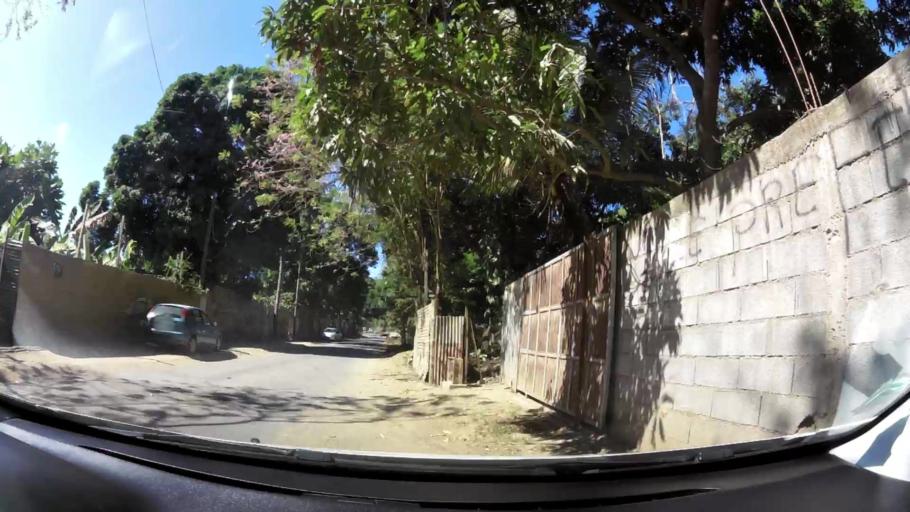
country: YT
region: Pamandzi
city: Pamandzi
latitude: -12.7828
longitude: 45.2834
